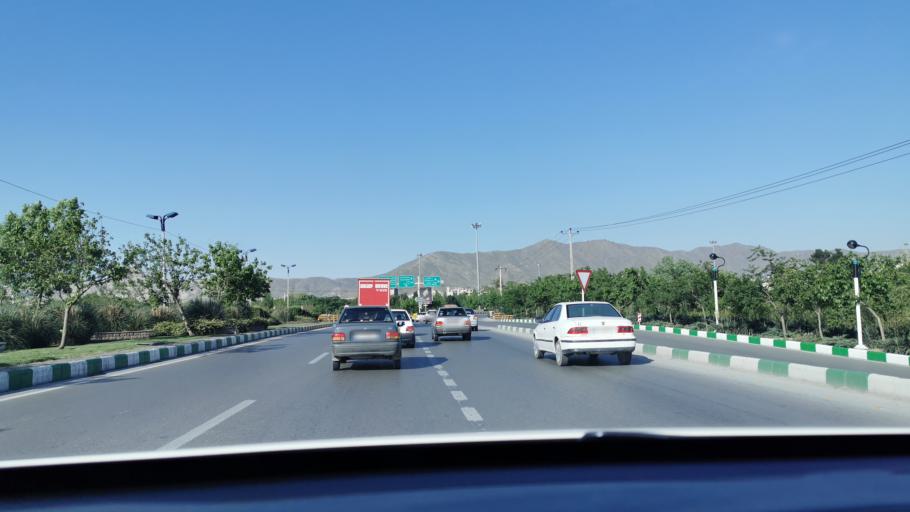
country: IR
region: Razavi Khorasan
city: Mashhad
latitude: 36.2518
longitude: 59.6129
